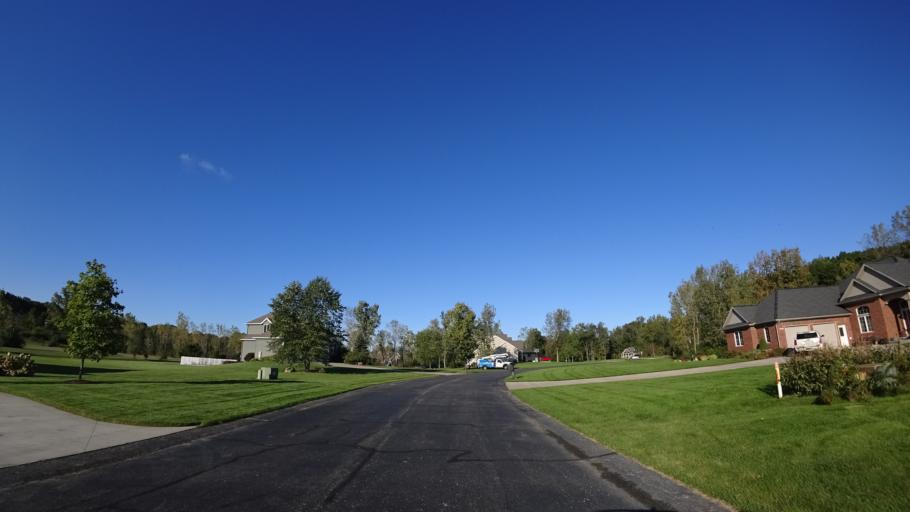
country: US
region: Michigan
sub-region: Kent County
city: Grandville
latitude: 42.9378
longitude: -85.7639
